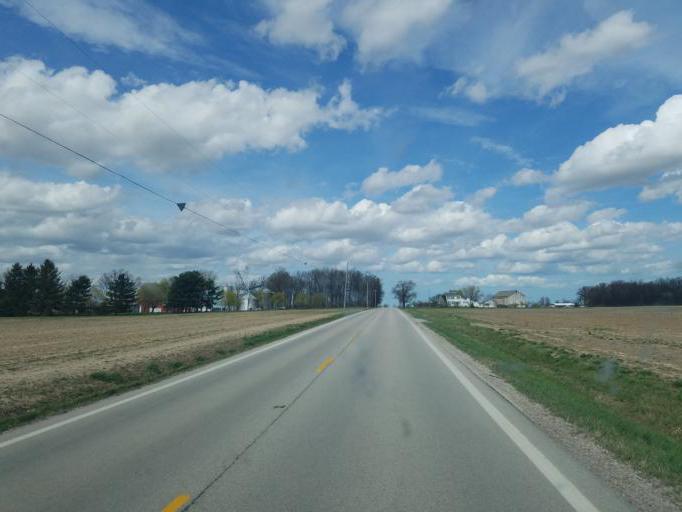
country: US
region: Ohio
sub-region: Huron County
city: Bellevue
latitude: 41.2450
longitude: -82.8040
